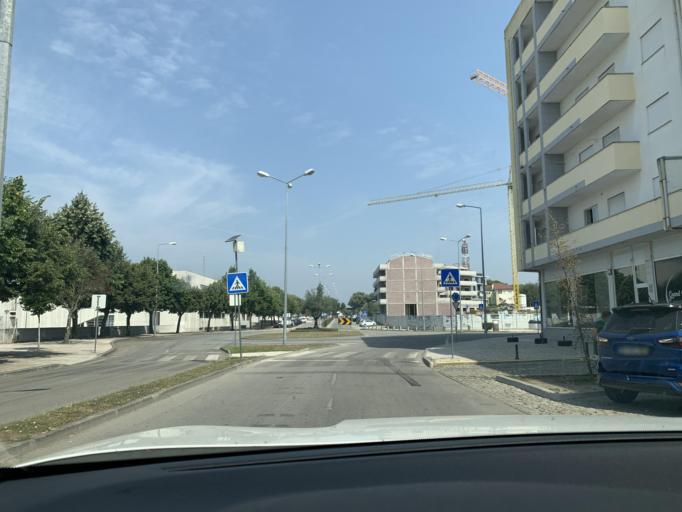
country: PT
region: Viseu
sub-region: Viseu
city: Viseu
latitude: 40.6460
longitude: -7.9185
